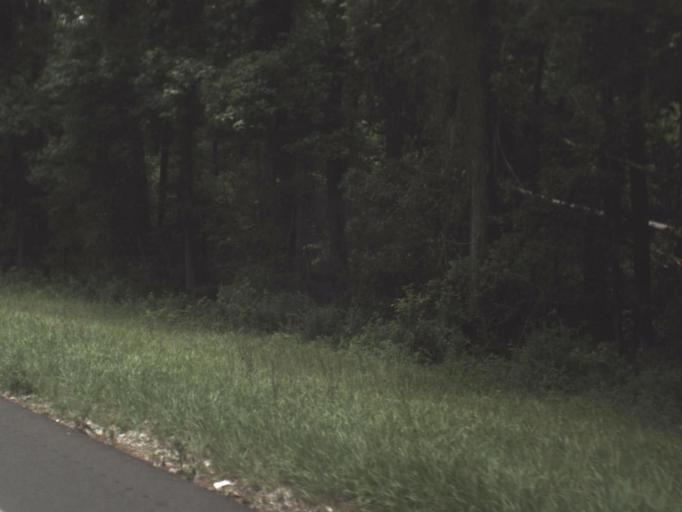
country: US
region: Florida
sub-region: Jefferson County
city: Monticello
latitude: 30.4732
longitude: -83.6629
